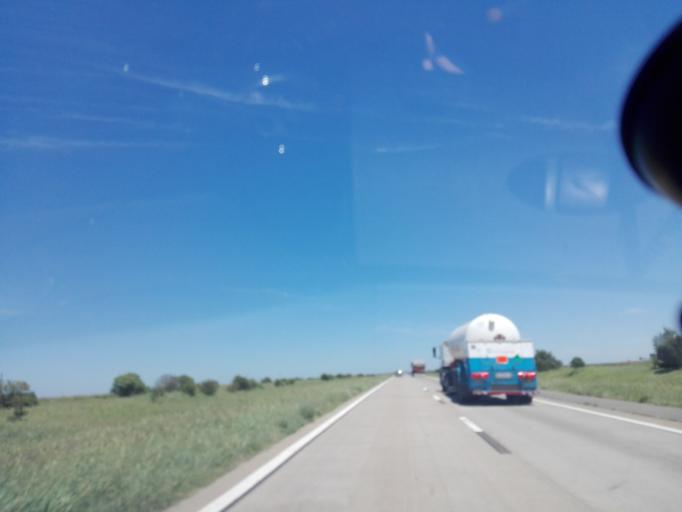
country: AR
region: Santa Fe
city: Armstrong
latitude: -32.8271
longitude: -61.5037
